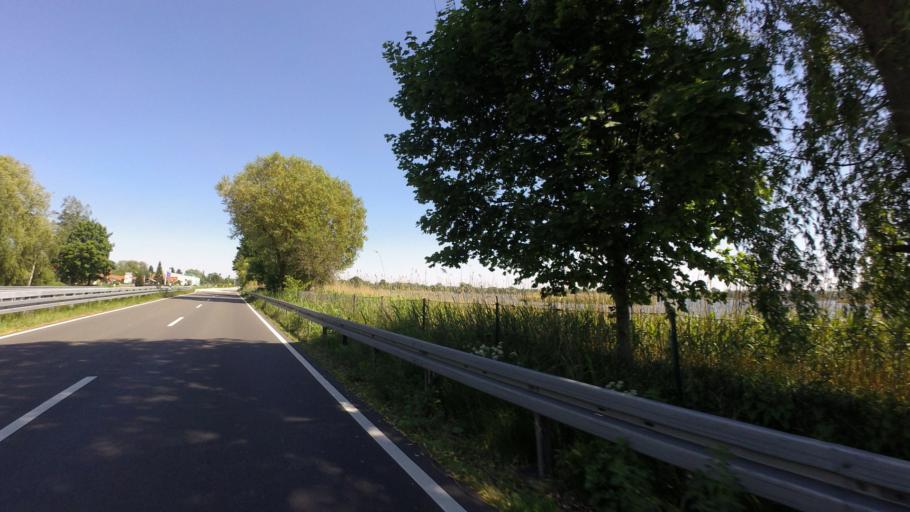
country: DE
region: Brandenburg
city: Peitz
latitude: 51.8482
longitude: 14.3955
